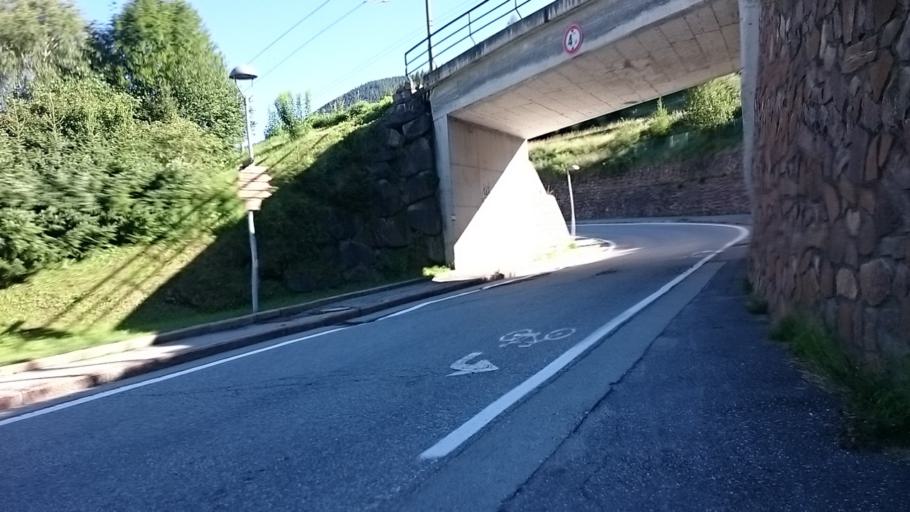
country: IT
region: Trentino-Alto Adige
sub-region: Bolzano
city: Monguelfo
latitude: 46.7544
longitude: 12.1035
